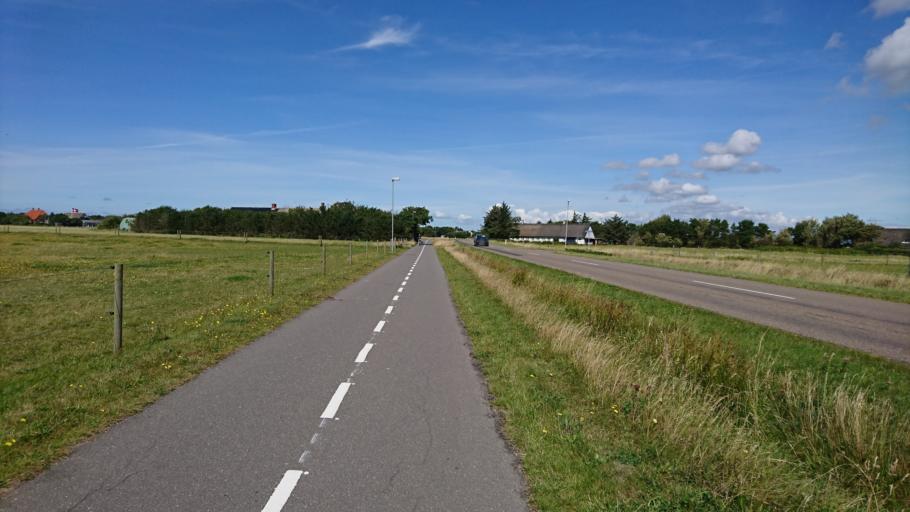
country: DK
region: South Denmark
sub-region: Fano Kommune
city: Nordby
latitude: 55.4270
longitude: 8.3968
